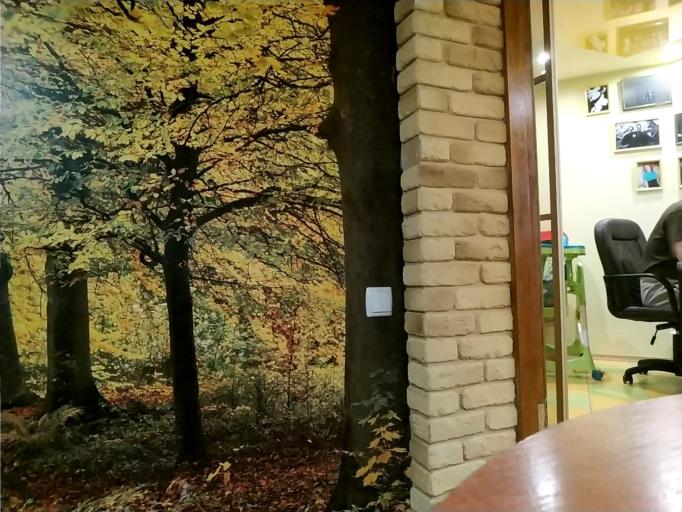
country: RU
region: Tverskaya
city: Staraya Toropa
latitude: 56.3353
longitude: 31.8715
